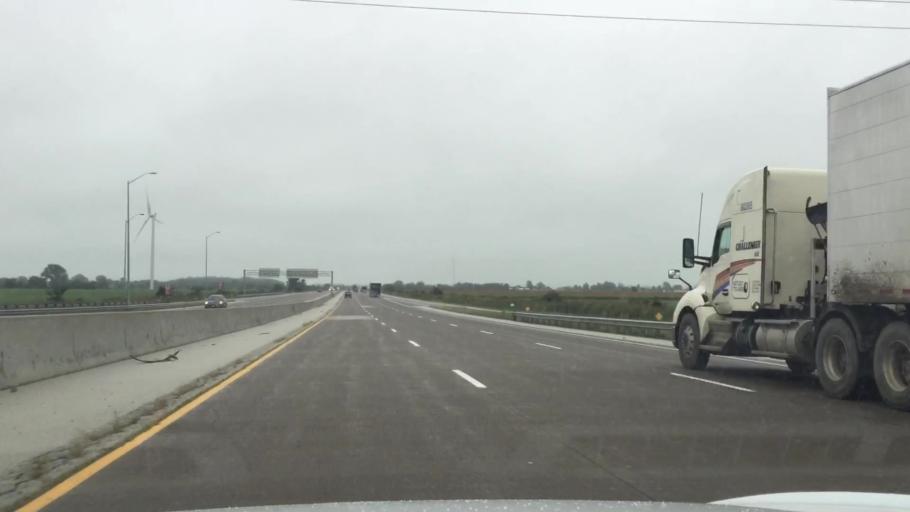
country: US
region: Michigan
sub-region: Wayne County
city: Grosse Pointe Farms
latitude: 42.2367
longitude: -82.7102
